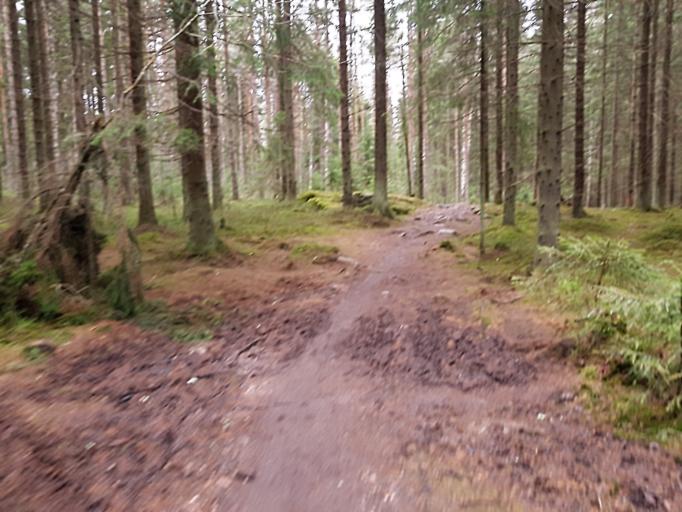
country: FI
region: Uusimaa
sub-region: Helsinki
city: Helsinki
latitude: 60.2610
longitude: 24.9209
